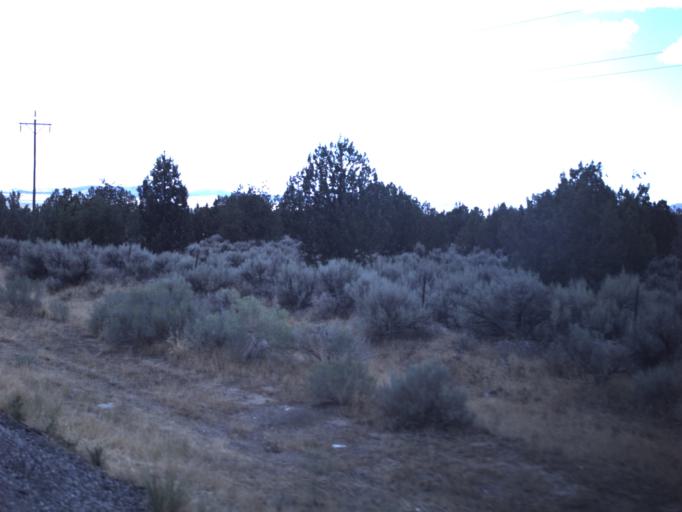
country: US
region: Utah
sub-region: Tooele County
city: Grantsville
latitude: 40.3110
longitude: -112.6375
